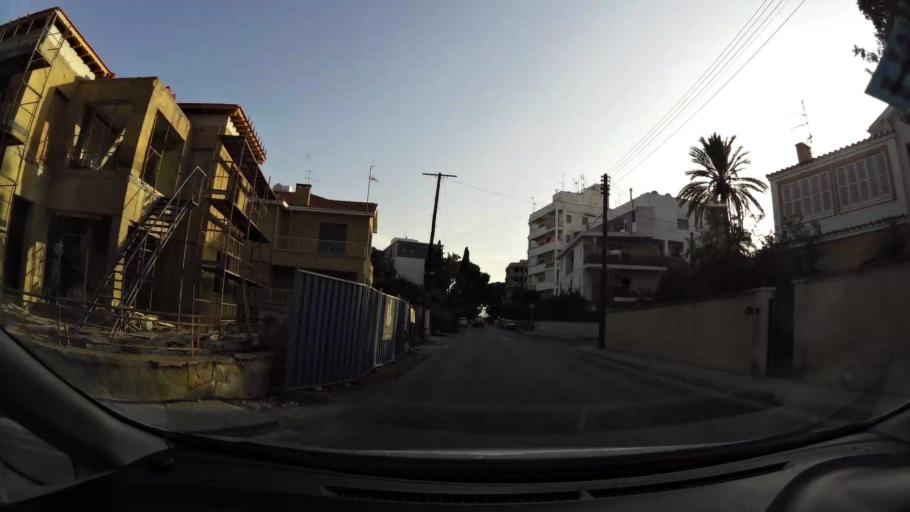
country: CY
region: Lefkosia
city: Nicosia
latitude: 35.1699
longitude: 33.3433
